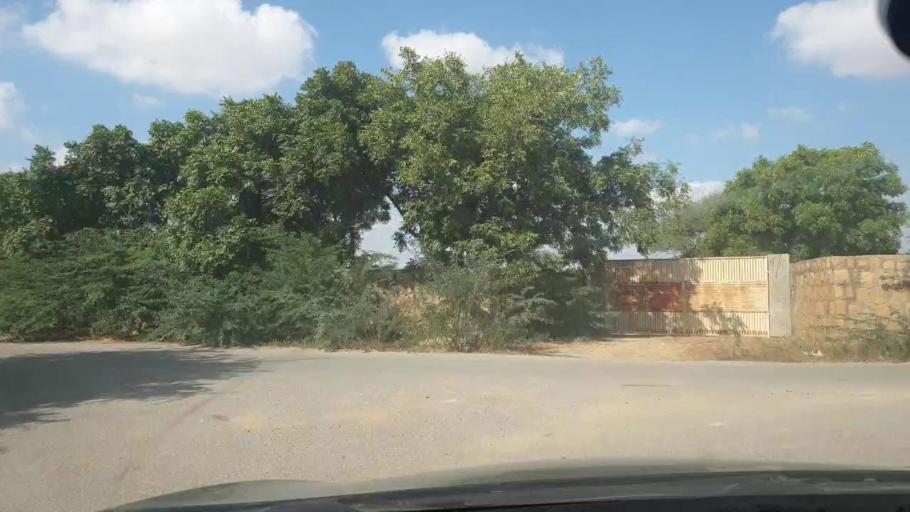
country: PK
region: Sindh
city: Malir Cantonment
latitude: 25.0531
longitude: 67.3887
